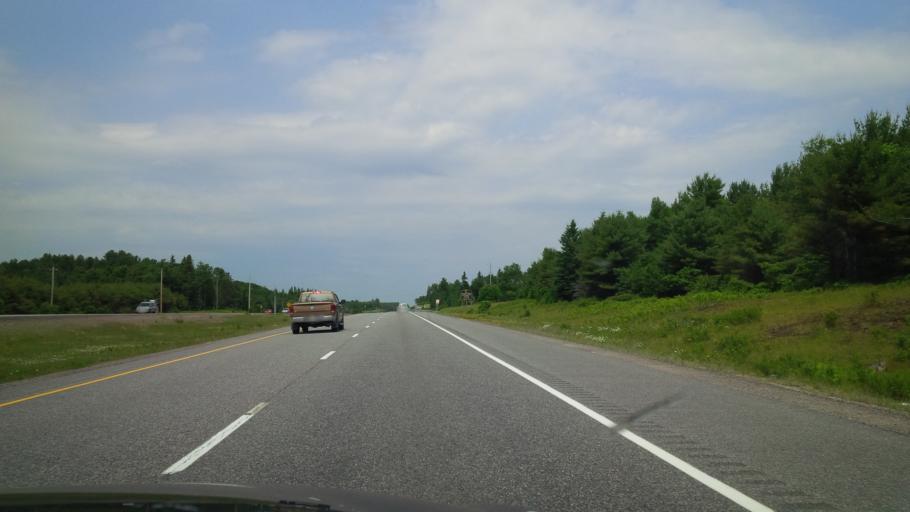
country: CA
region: Ontario
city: Huntsville
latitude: 45.4839
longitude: -79.2801
